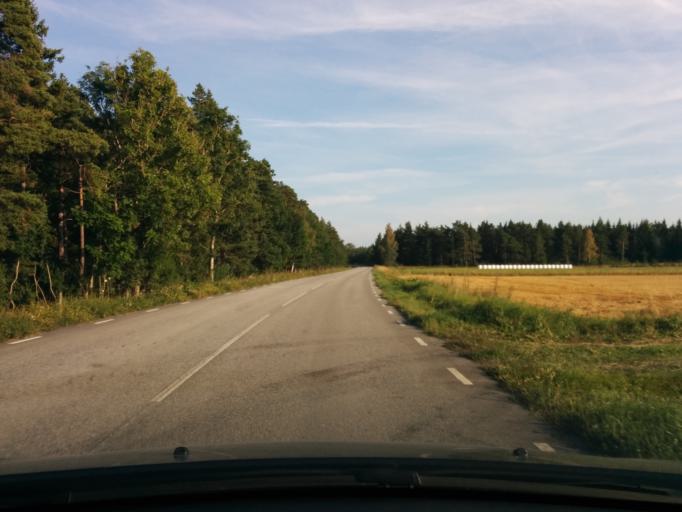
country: SE
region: Gotland
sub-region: Gotland
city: Visby
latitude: 57.5241
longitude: 18.5417
